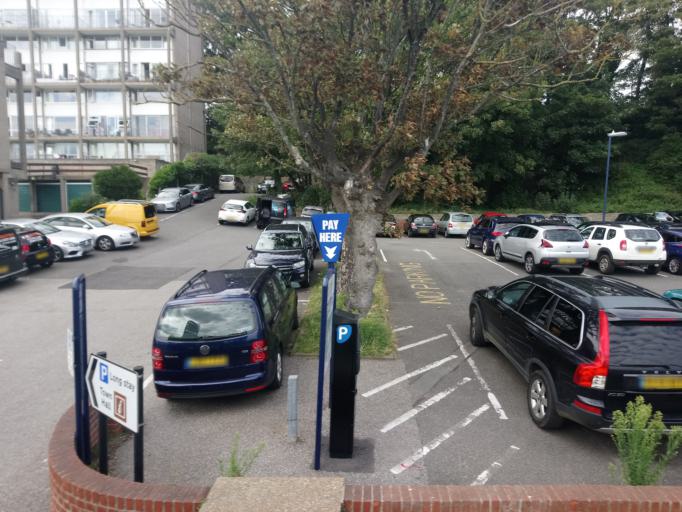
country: GB
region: England
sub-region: Suffolk
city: Felixstowe
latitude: 51.9588
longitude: 1.3472
